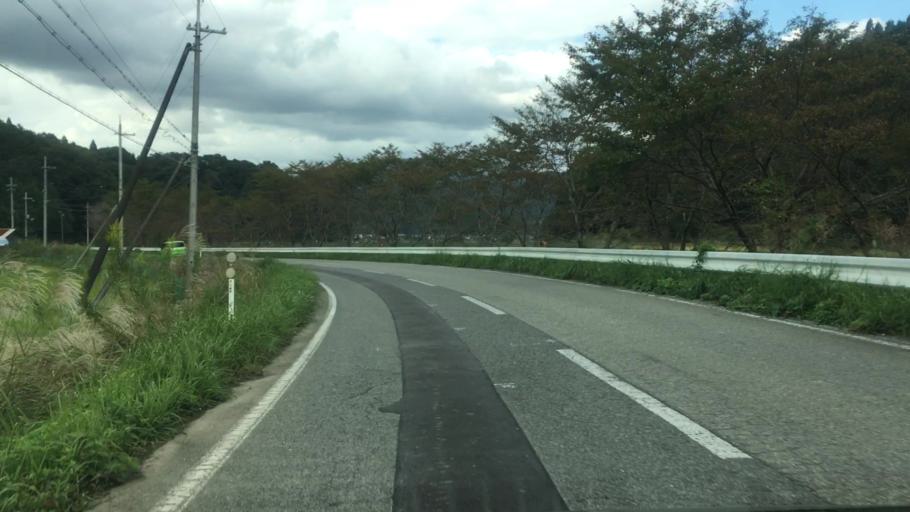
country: JP
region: Hyogo
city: Toyooka
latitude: 35.4421
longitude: 134.7315
